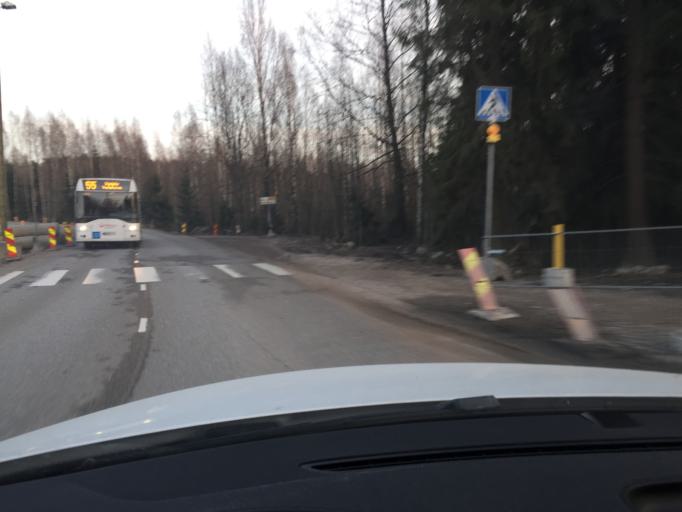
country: FI
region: Uusimaa
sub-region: Helsinki
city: Helsinki
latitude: 60.2811
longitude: 24.9235
